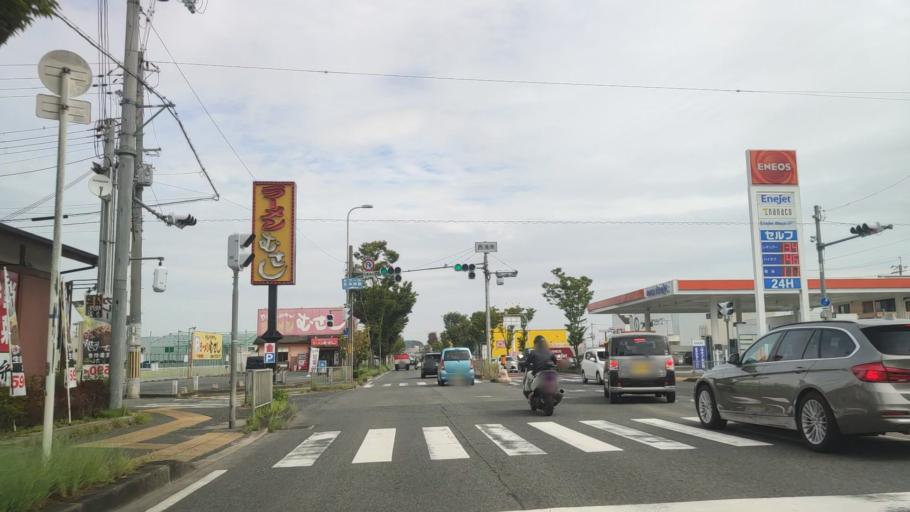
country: JP
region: Osaka
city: Tondabayashicho
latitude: 34.5372
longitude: 135.6047
